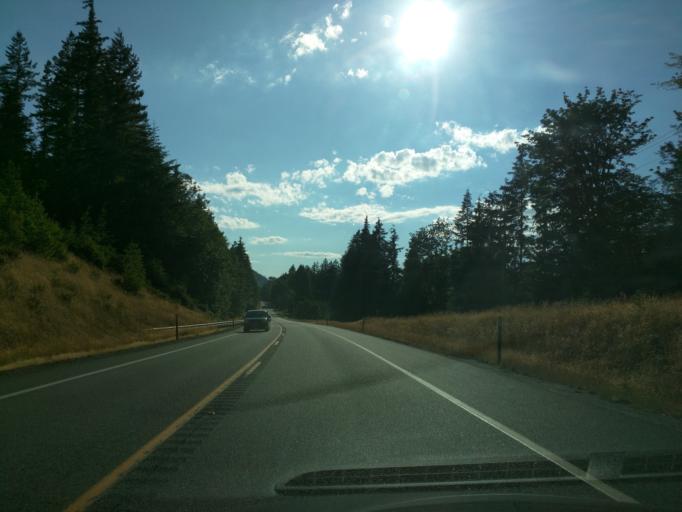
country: US
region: Washington
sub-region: Snohomish County
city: Darrington
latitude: 48.2788
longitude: -121.7724
